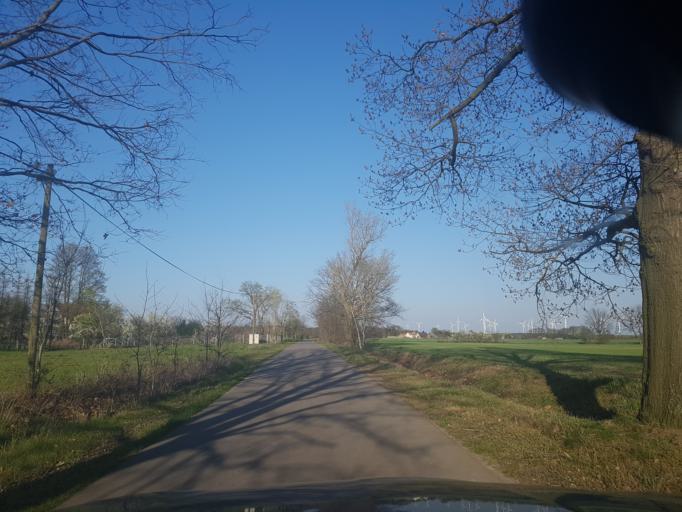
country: DE
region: Brandenburg
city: Falkenberg
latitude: 51.5253
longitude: 13.2739
